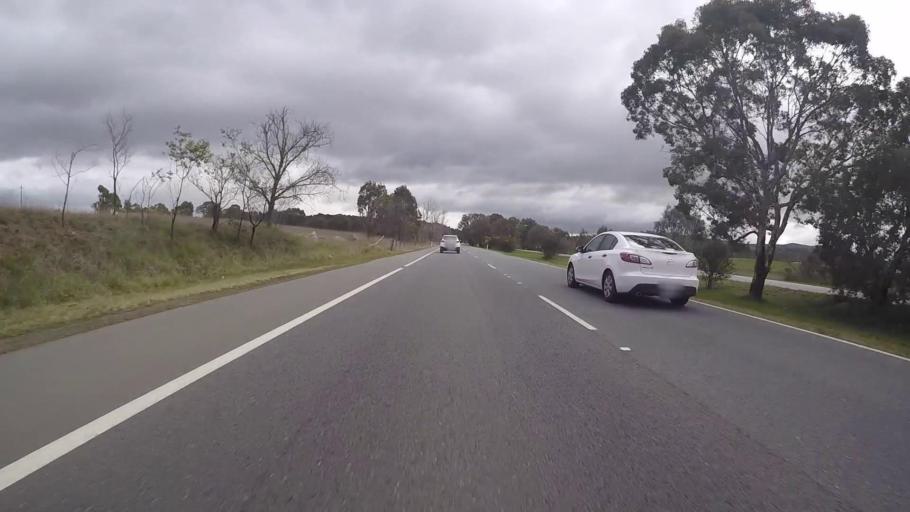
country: AU
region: Australian Capital Territory
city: Kaleen
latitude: -35.2073
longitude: 149.1039
